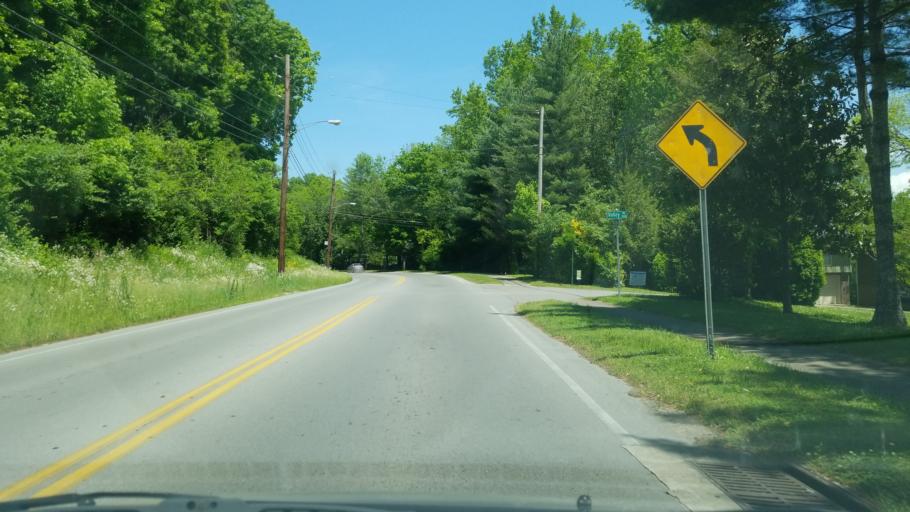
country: US
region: Tennessee
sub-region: Hamilton County
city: Red Bank
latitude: 35.1240
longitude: -85.3119
